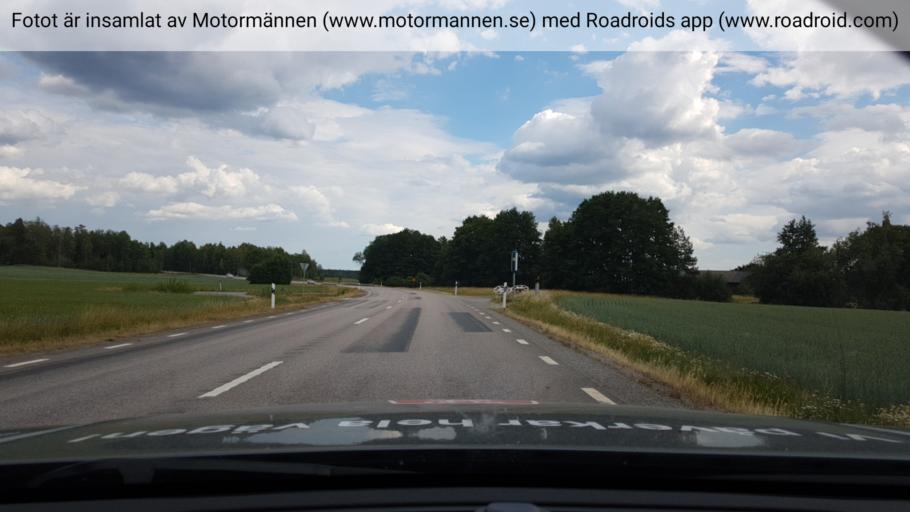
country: SE
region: Uppsala
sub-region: Heby Kommun
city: Morgongava
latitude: 59.9193
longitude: 16.9958
